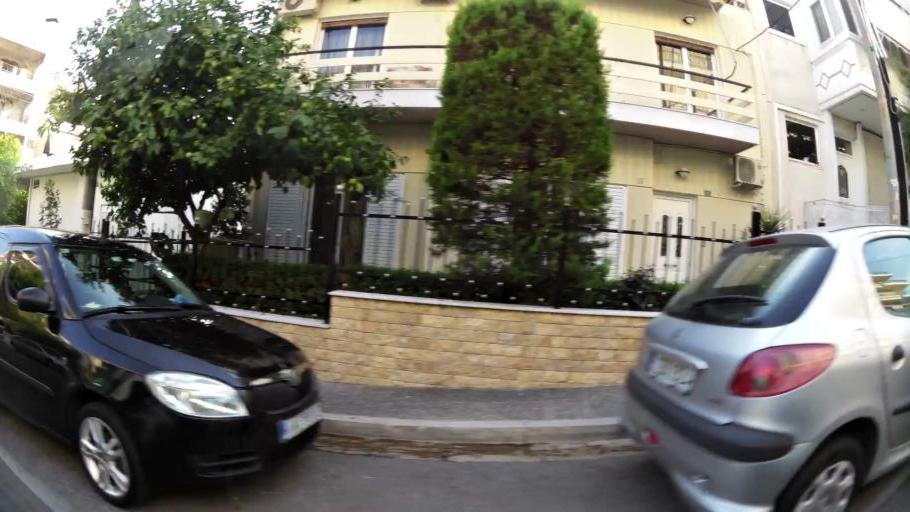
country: GR
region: Attica
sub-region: Nomarchia Athinas
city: Petroupolis
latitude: 38.0424
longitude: 23.6749
